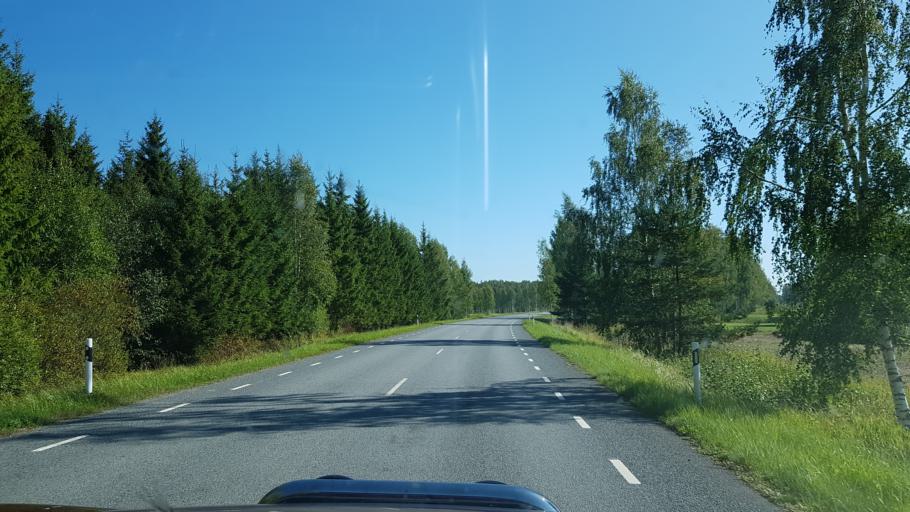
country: EE
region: Polvamaa
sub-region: Polva linn
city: Polva
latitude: 58.2772
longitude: 27.1032
